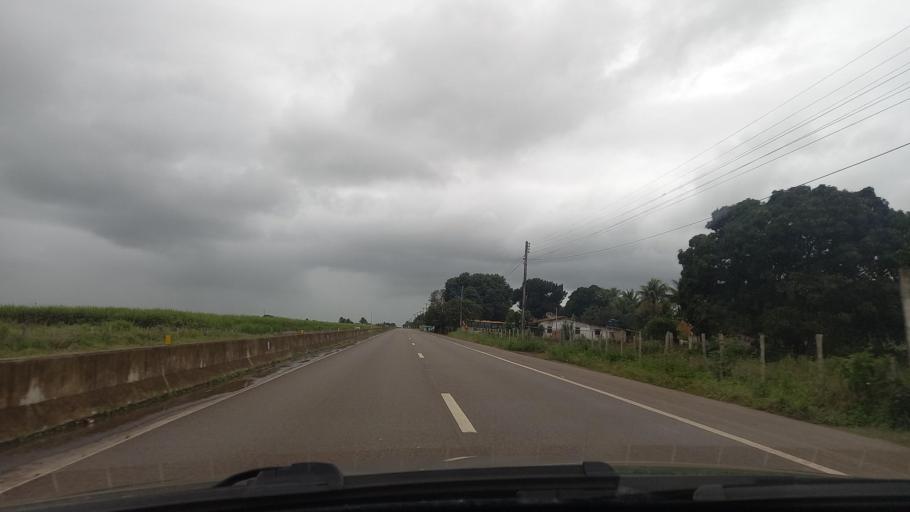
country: BR
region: Alagoas
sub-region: Limoeiro De Anadia
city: Cajueiro
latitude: -9.7576
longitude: -36.4420
